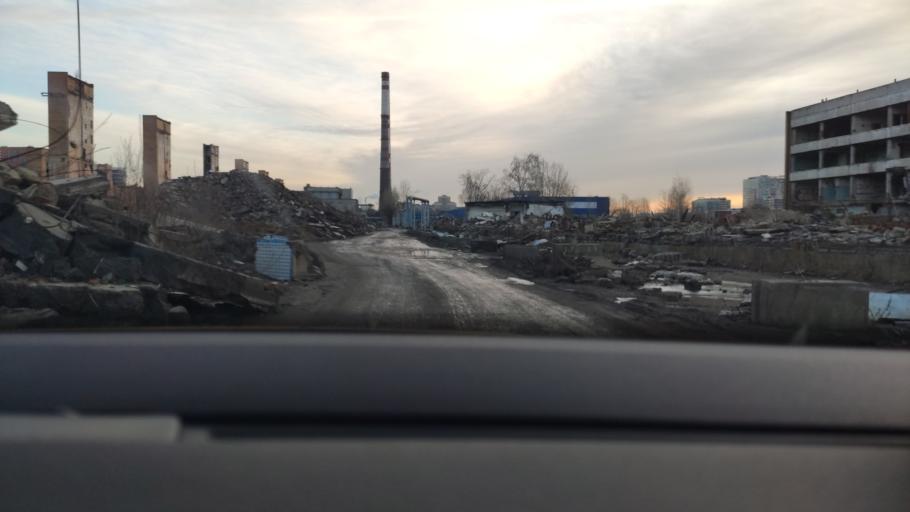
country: RU
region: Moskovskaya
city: Kozhukhovo
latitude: 55.6919
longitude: 37.6450
